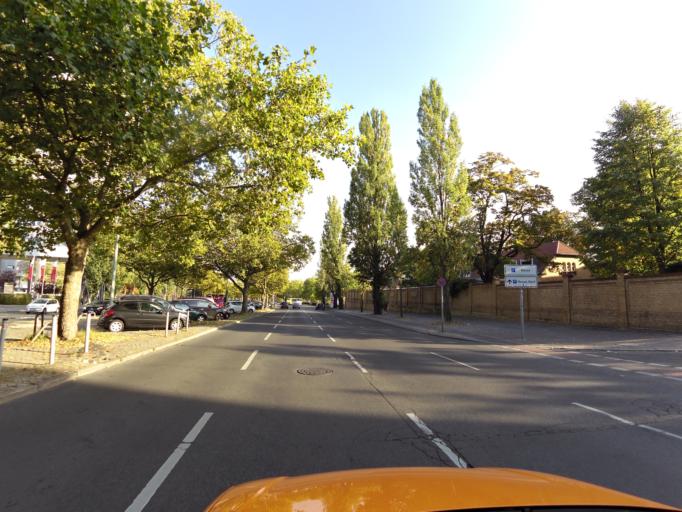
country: DE
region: Berlin
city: Westend
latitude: 52.5087
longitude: 13.2733
